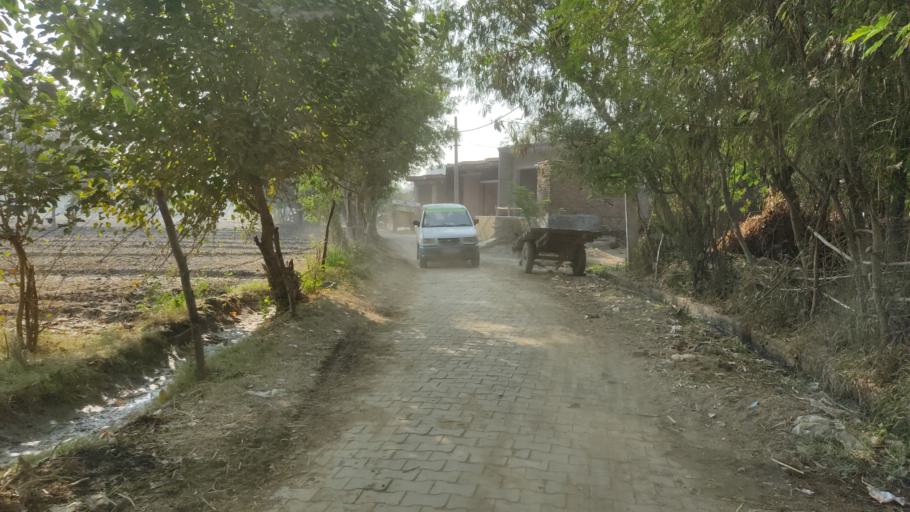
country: IN
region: Uttar Pradesh
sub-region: Mathura
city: Radha Kund
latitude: 27.5615
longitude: 77.5576
